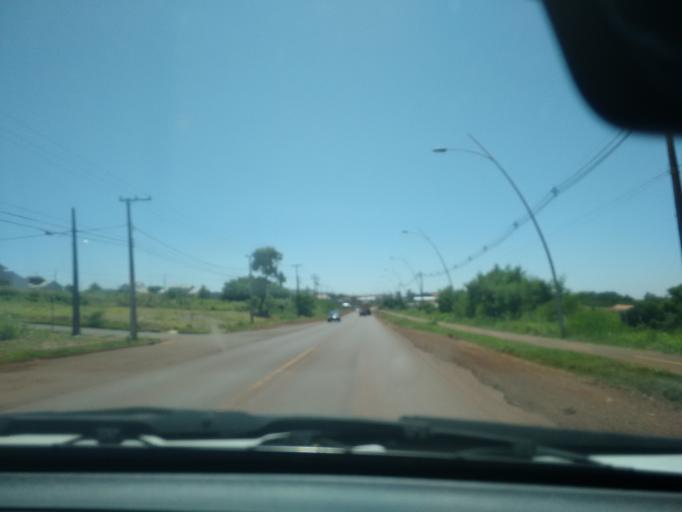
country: BR
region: Parana
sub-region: Marechal Candido Rondon
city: Marechal Candido Rondon
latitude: -24.5569
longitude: -54.0945
